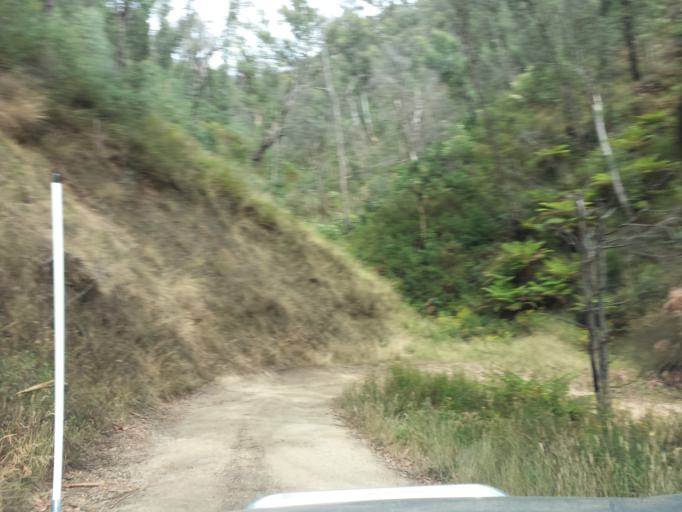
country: AU
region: Victoria
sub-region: Latrobe
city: Moe
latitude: -37.7591
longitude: 146.3971
